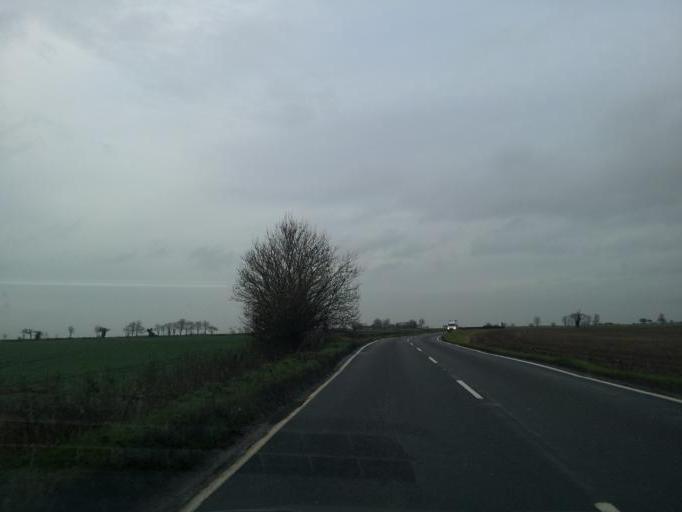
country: GB
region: England
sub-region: Norfolk
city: Martham
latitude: 52.6756
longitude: 1.5933
